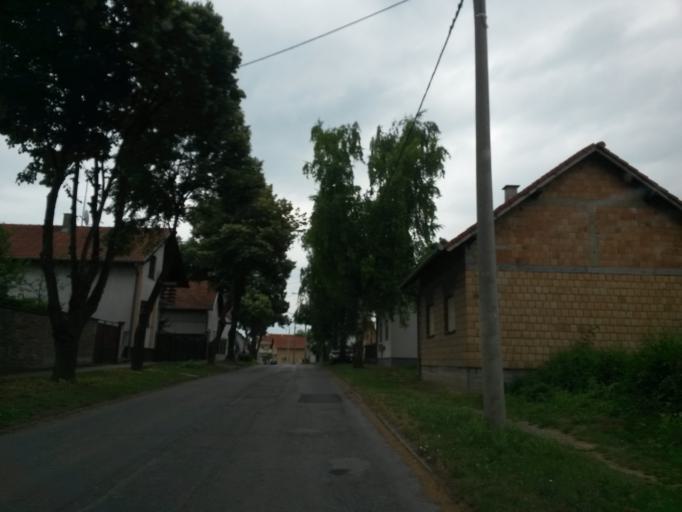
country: HR
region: Vukovarsko-Srijemska
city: Vukovar
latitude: 45.3451
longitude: 18.9955
